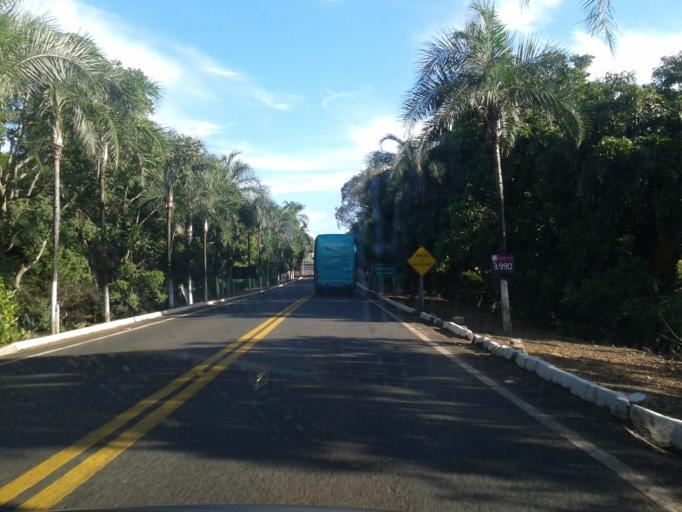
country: BR
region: Minas Gerais
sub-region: Tupaciguara
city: Tupaciguara
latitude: -18.3174
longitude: -48.5628
